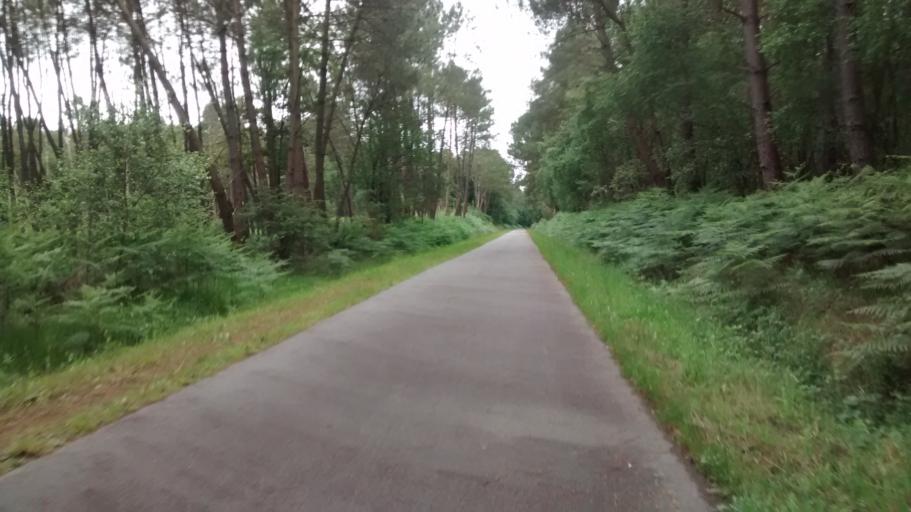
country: FR
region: Brittany
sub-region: Departement du Morbihan
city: Molac
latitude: 47.7406
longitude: -2.4101
